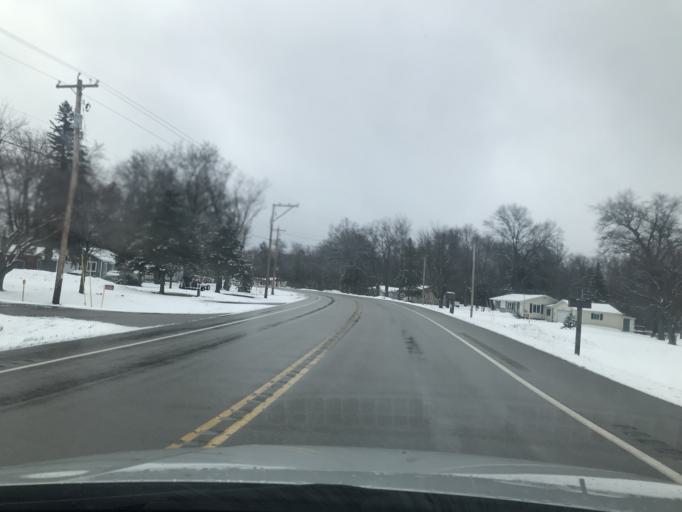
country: US
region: Wisconsin
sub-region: Marinette County
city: Peshtigo
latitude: 45.1735
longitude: -87.7389
